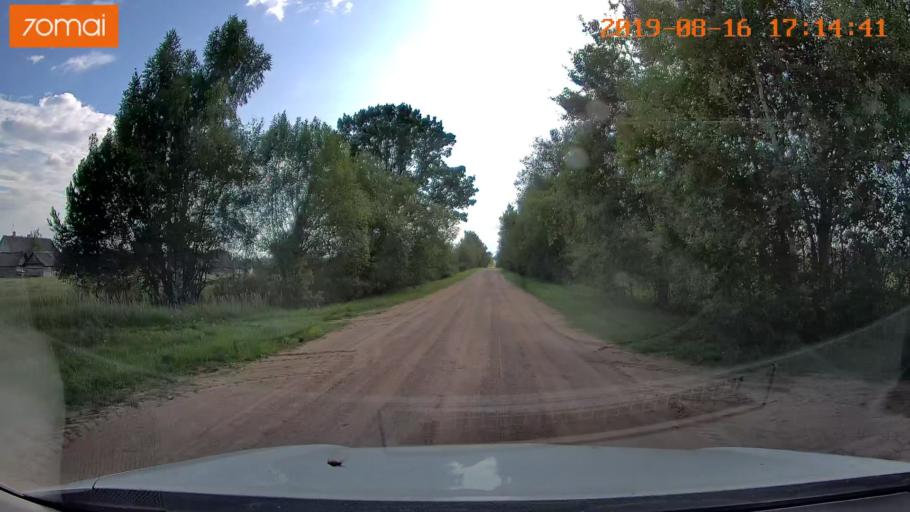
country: BY
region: Mogilev
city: Hlusha
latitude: 53.1828
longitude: 28.8547
